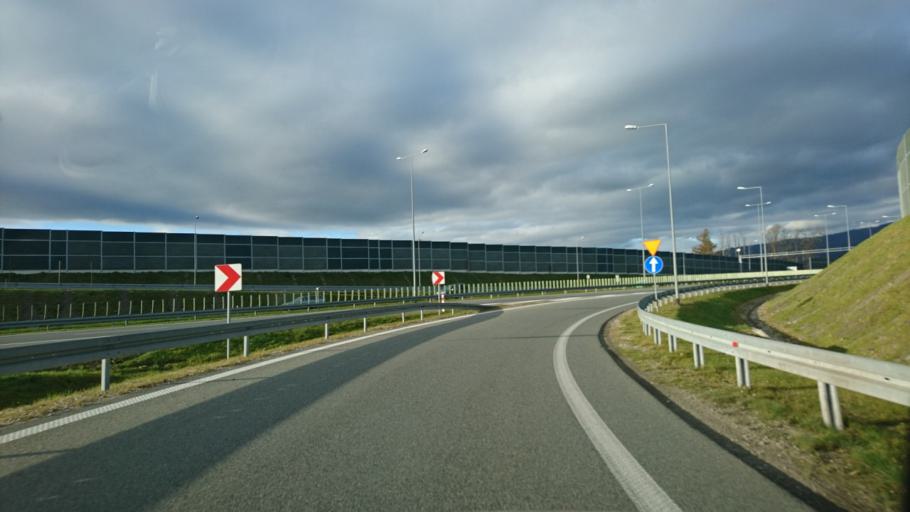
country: PL
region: Silesian Voivodeship
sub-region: Powiat zywiecki
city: Lodygowice
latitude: 49.7129
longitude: 19.1220
